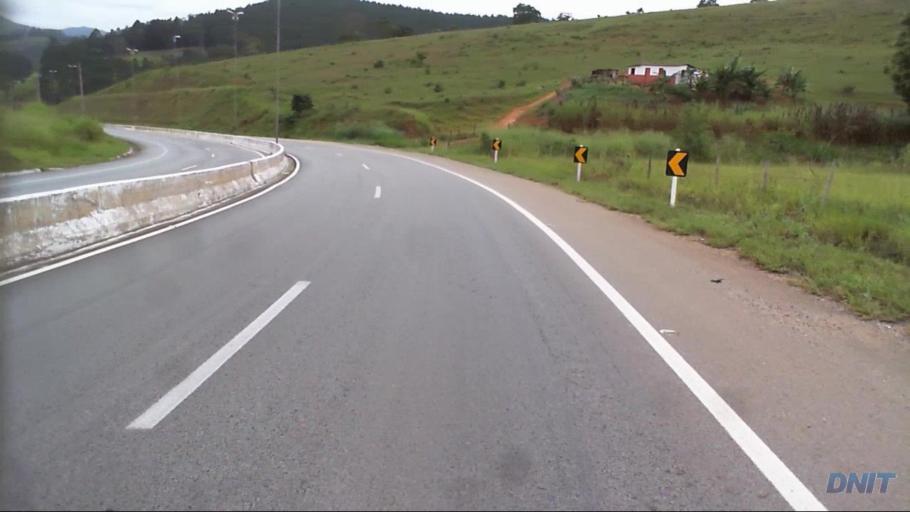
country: BR
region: Minas Gerais
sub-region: Nova Era
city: Nova Era
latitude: -19.7621
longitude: -43.0480
